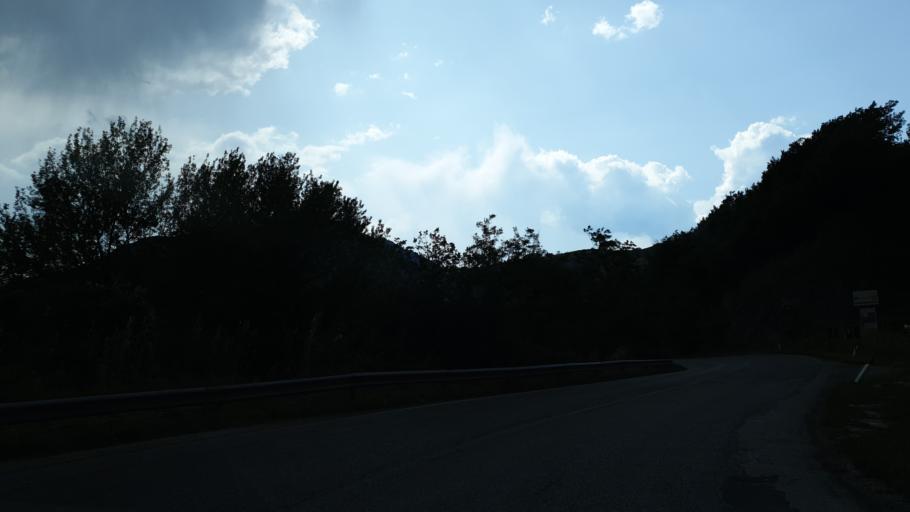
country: IT
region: Emilia-Romagna
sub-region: Provincia di Rimini
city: Talamello
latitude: 43.9100
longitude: 12.3028
